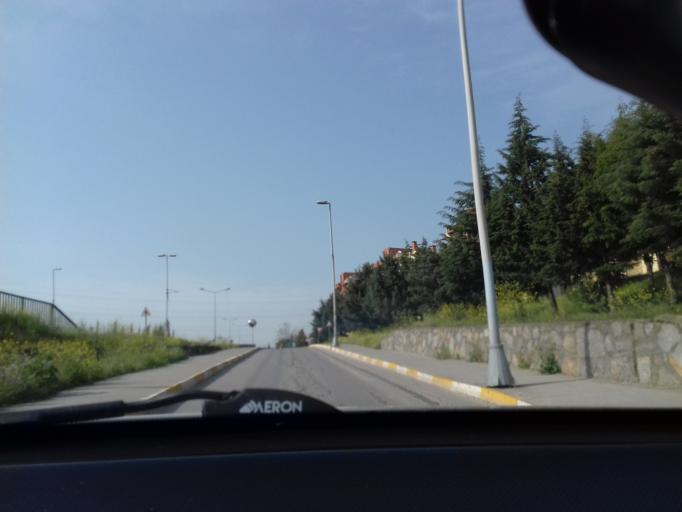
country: TR
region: Istanbul
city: Pendik
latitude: 40.9060
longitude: 29.2755
